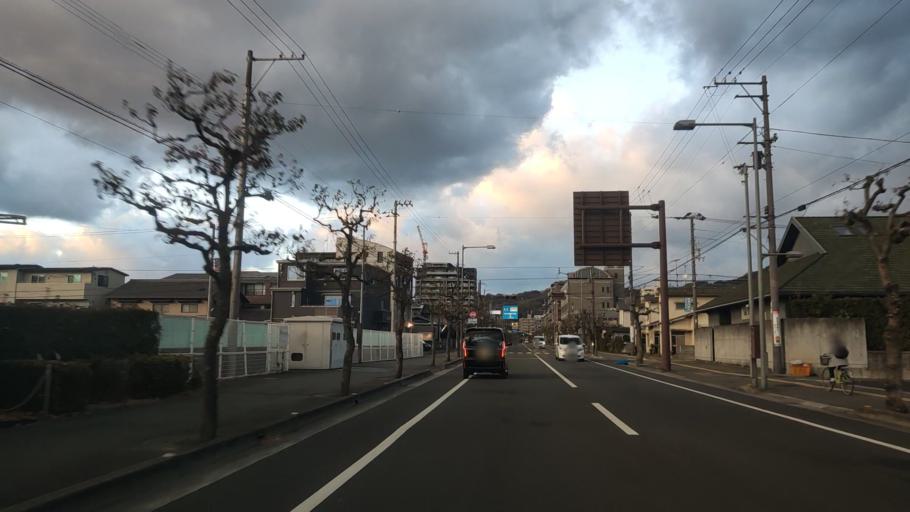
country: JP
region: Ehime
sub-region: Shikoku-chuo Shi
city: Matsuyama
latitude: 33.8437
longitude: 132.7844
